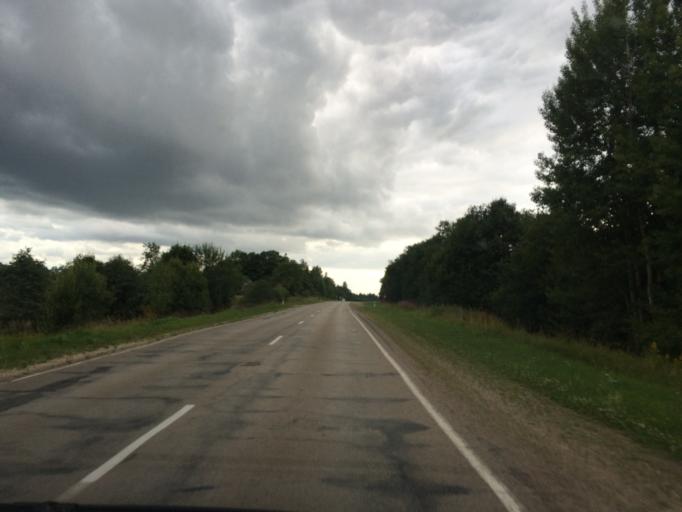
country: LV
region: Rezekne
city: Rezekne
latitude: 56.5883
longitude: 27.4058
